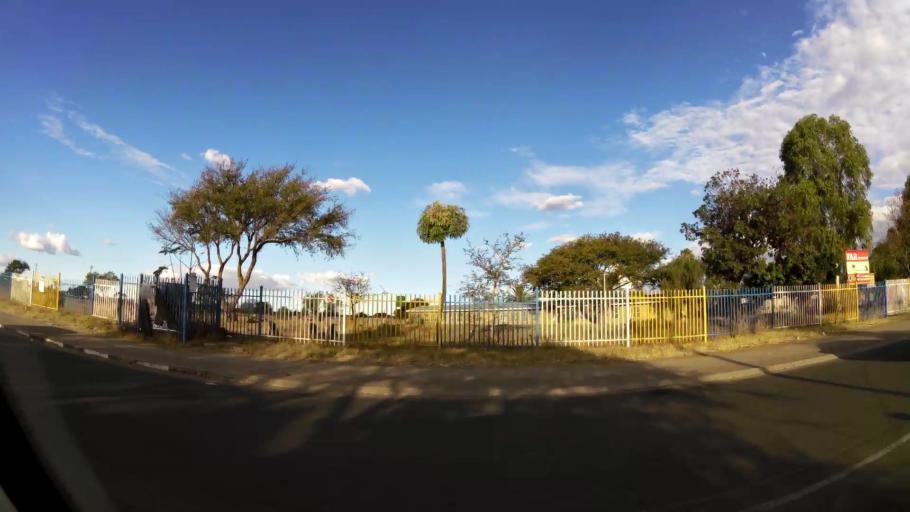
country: ZA
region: Limpopo
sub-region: Capricorn District Municipality
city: Polokwane
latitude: -23.9074
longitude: 29.4291
